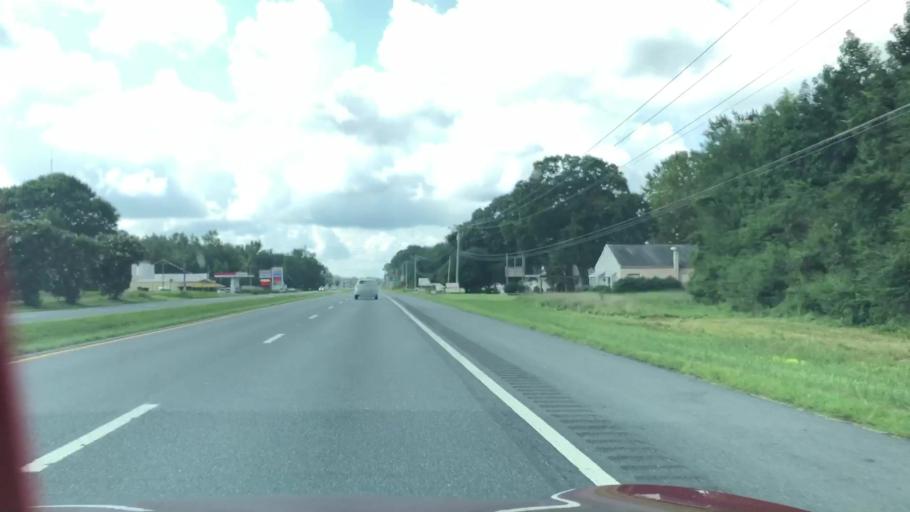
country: US
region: Virginia
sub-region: Accomack County
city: Wattsville
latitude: 37.9548
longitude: -75.5357
